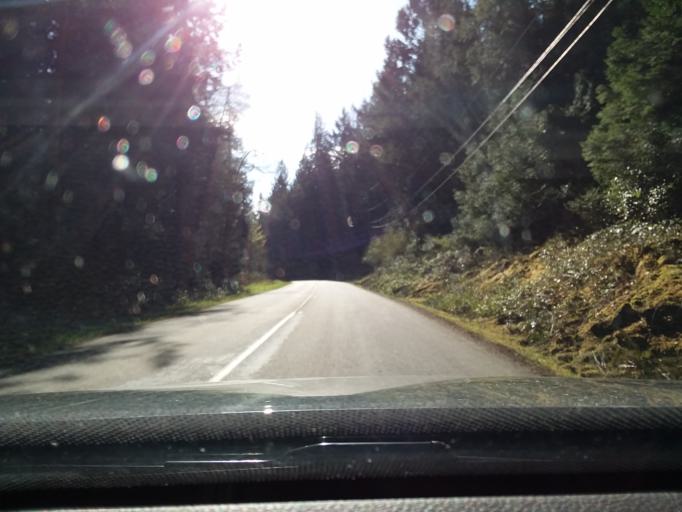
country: CA
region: British Columbia
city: North Cowichan
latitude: 48.9486
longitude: -123.5189
